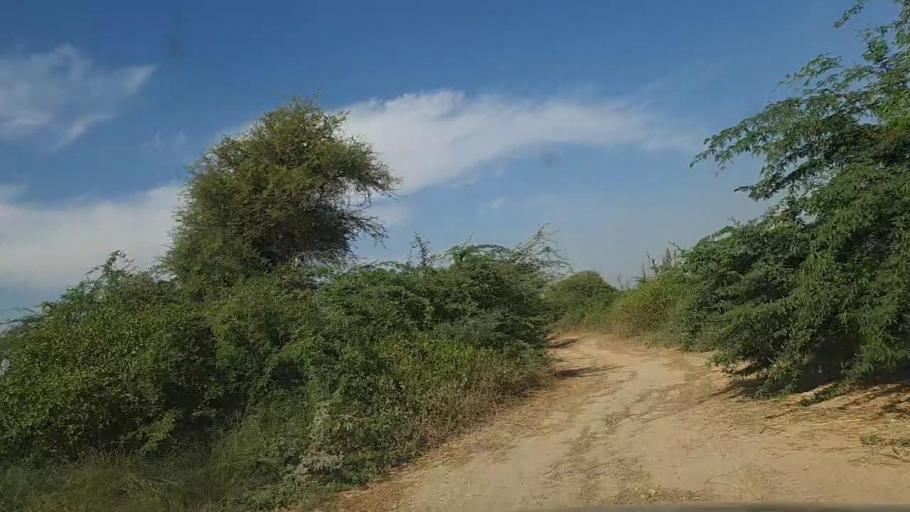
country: PK
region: Sindh
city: Bulri
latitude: 24.8222
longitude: 68.2670
